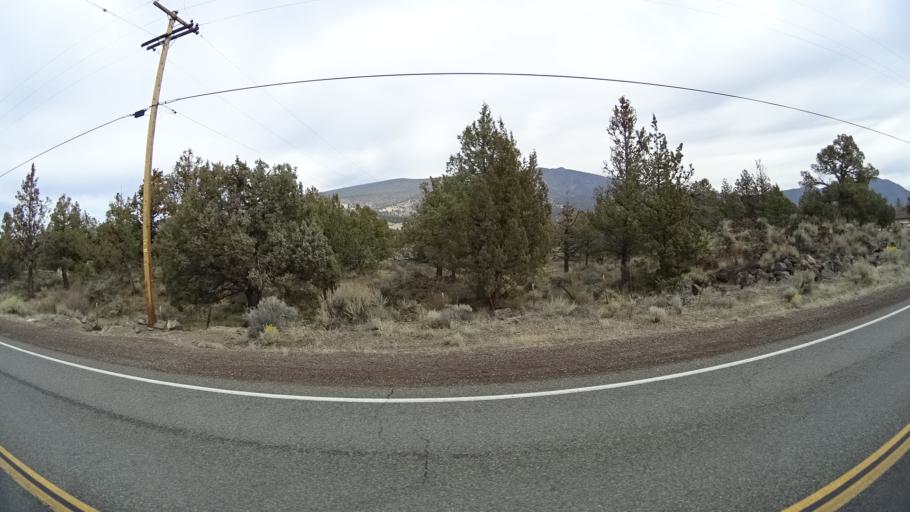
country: US
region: California
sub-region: Siskiyou County
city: Weed
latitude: 41.5898
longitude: -122.3034
